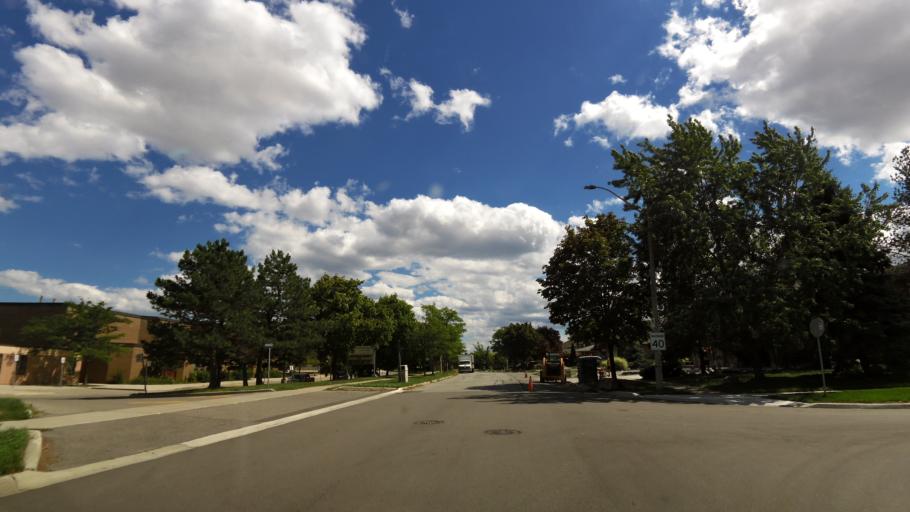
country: CA
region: Ontario
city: Mississauga
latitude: 43.6135
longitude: -79.6229
